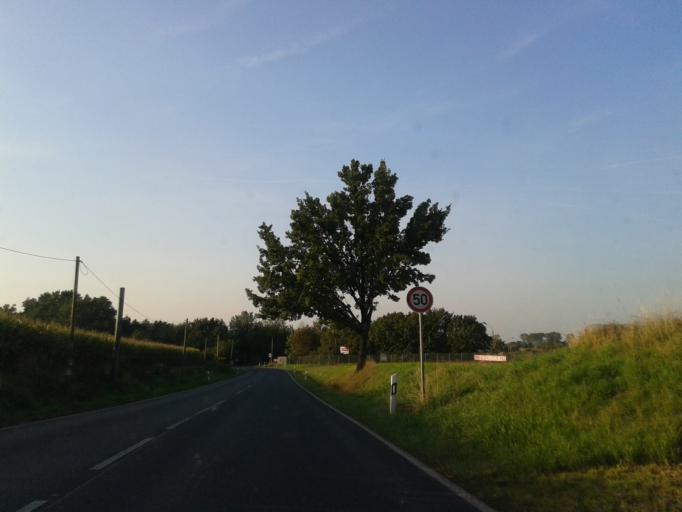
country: DE
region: Saxony
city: Klipphausen
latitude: 51.0984
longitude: 13.4956
